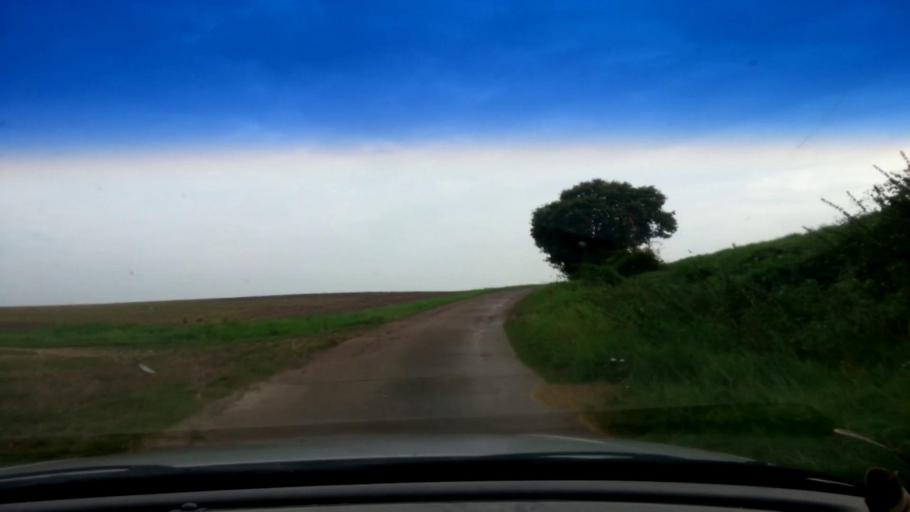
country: DE
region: Bavaria
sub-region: Upper Franconia
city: Rattelsdorf
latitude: 50.0590
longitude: 10.8833
